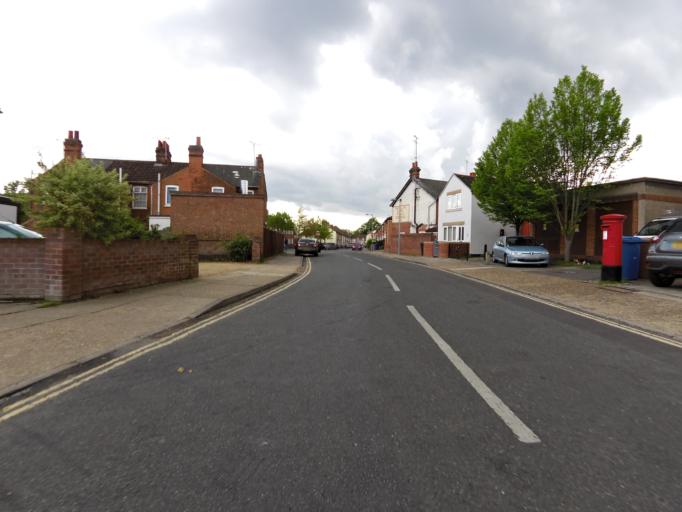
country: GB
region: England
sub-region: Suffolk
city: Ipswich
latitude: 52.0615
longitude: 1.1650
